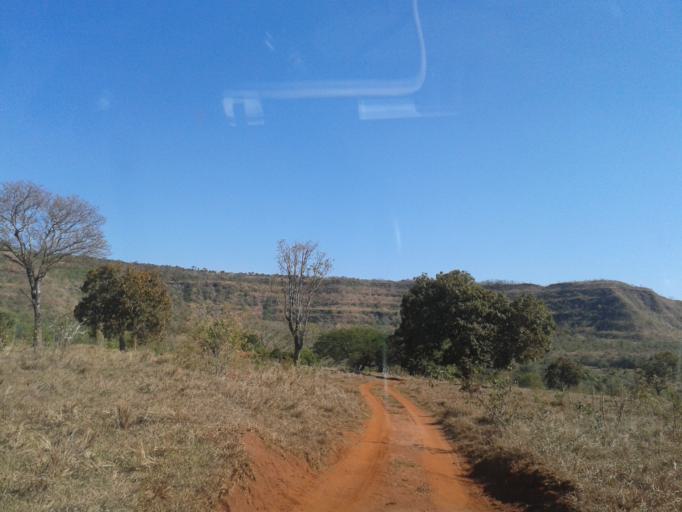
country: BR
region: Minas Gerais
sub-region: Santa Vitoria
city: Santa Vitoria
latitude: -19.0893
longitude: -49.9676
